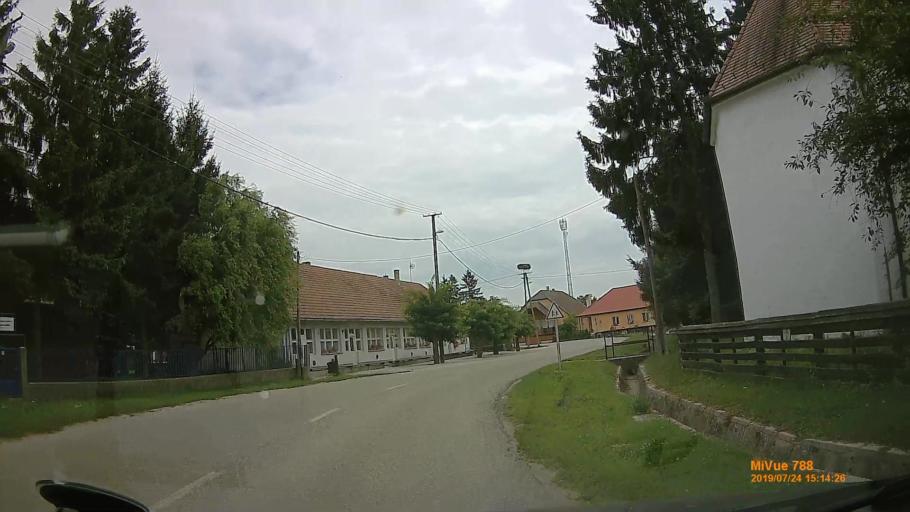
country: HU
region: Szabolcs-Szatmar-Bereg
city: Tarpa
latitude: 48.1996
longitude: 22.5248
